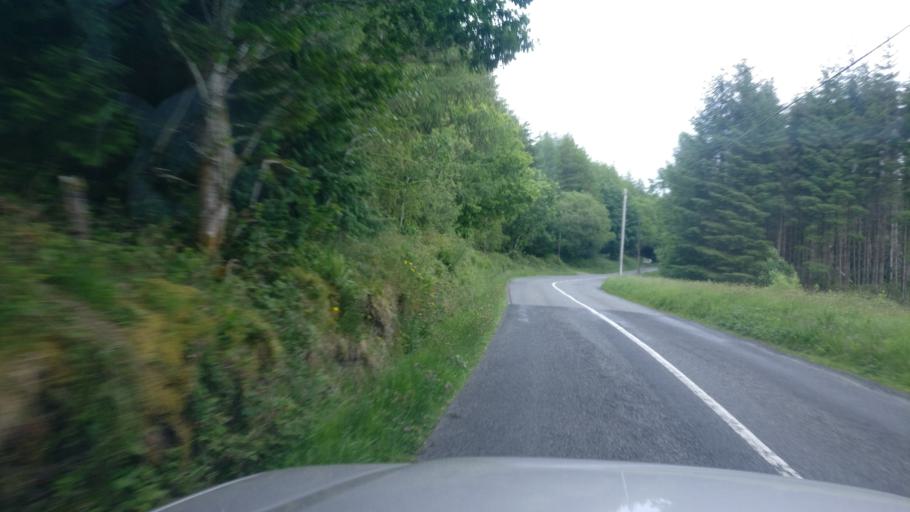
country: IE
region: Connaught
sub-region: County Galway
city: Gort
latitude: 53.0558
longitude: -8.6545
